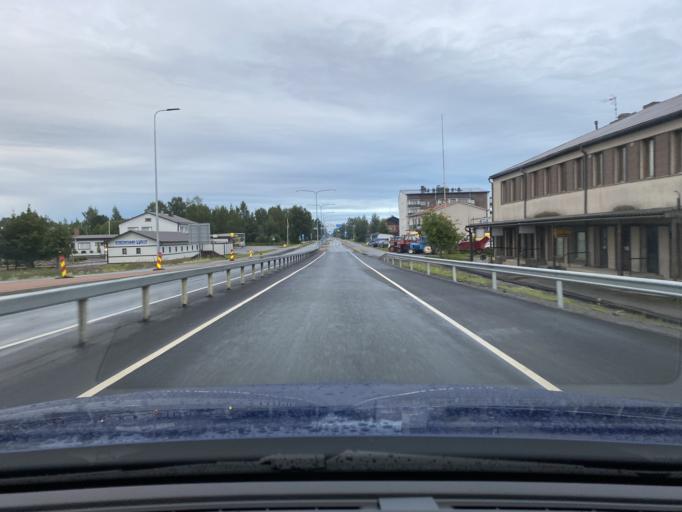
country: FI
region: Ostrobothnia
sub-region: Kyroenmaa
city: Laihia
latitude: 62.9821
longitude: 22.0050
